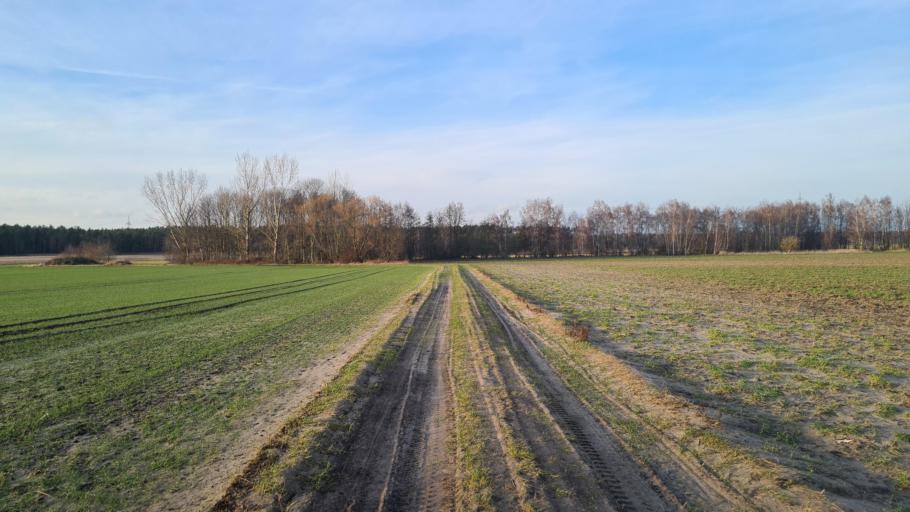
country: DE
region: Brandenburg
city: Schonborn
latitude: 51.5454
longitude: 13.4670
